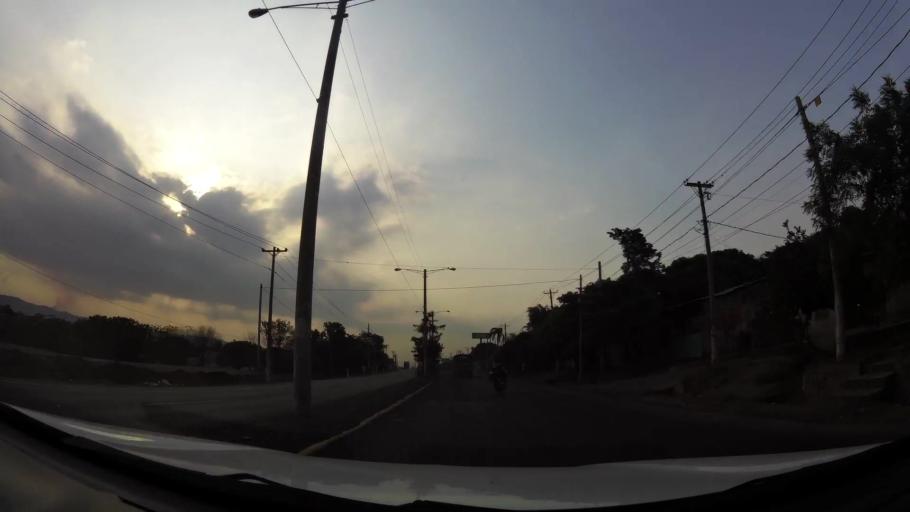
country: NI
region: Managua
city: Ciudad Sandino
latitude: 12.1717
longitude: -86.3448
